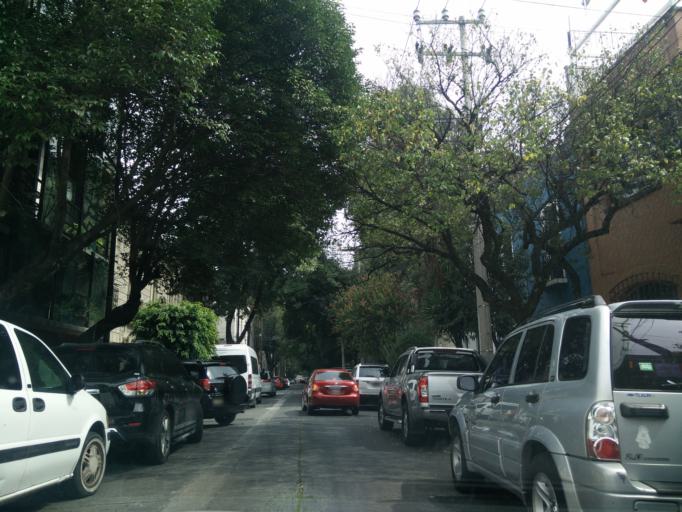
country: MX
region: Mexico City
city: Polanco
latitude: 19.4140
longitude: -99.1861
